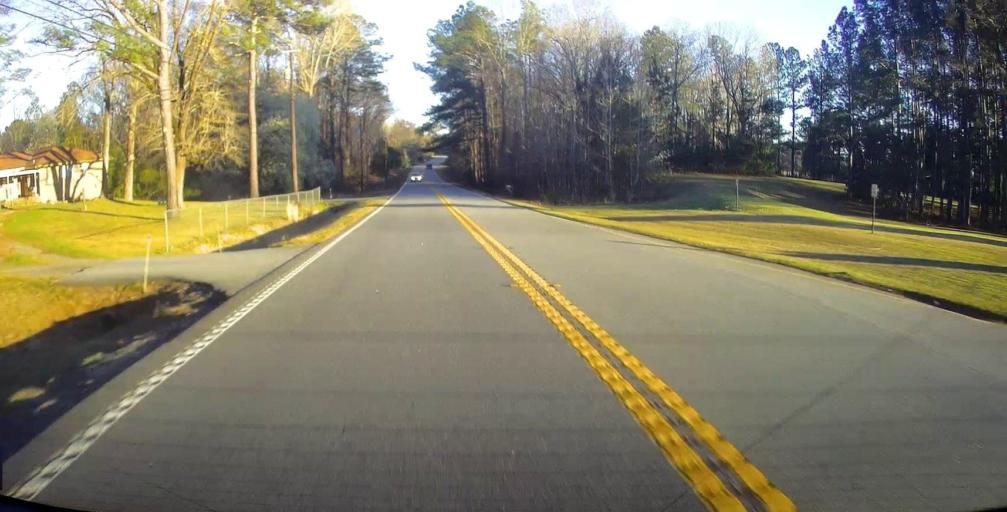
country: US
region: Georgia
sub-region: Harris County
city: Hamilton
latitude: 32.6313
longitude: -84.8255
